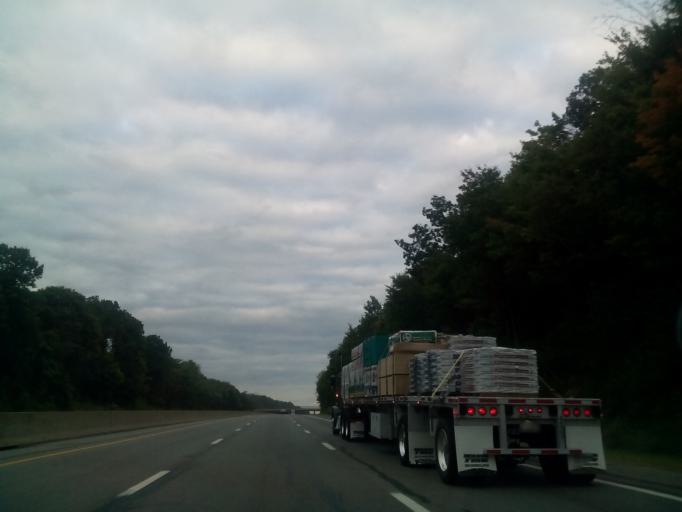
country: US
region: Ohio
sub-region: Portage County
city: Garrettsville
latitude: 41.2441
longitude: -81.0912
